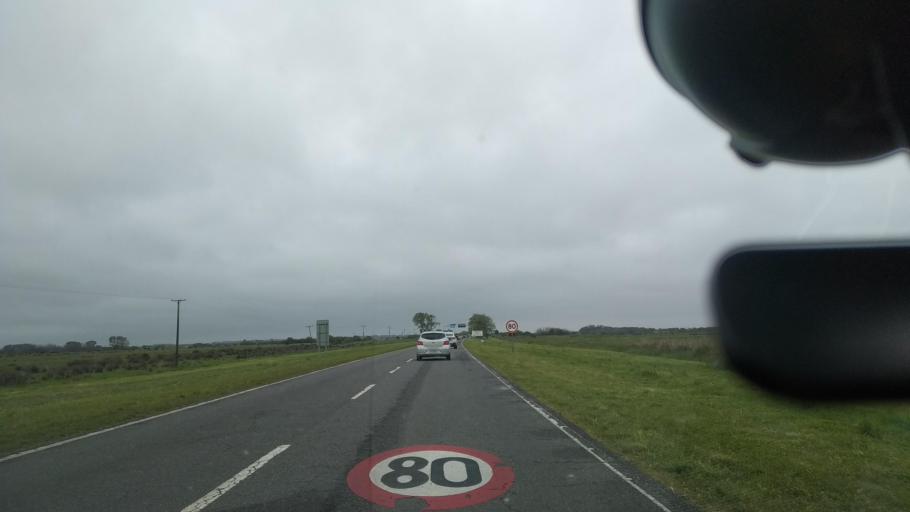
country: AR
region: Buenos Aires
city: Veronica
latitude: -35.5979
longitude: -57.2729
